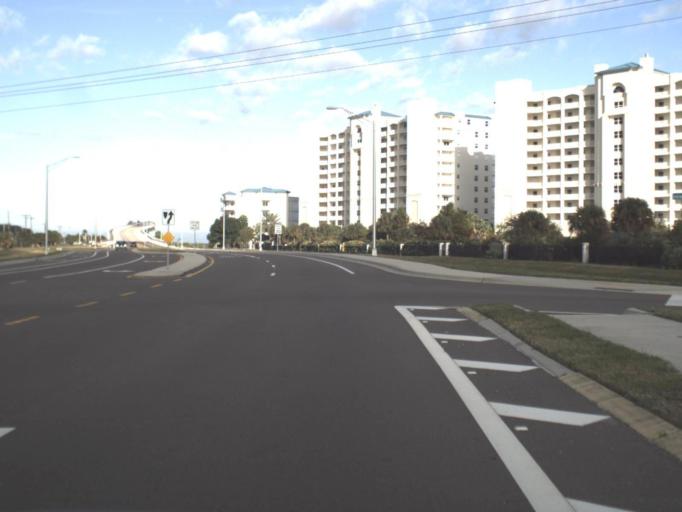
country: US
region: Florida
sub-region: Brevard County
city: Titusville
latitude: 28.6156
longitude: -80.8059
